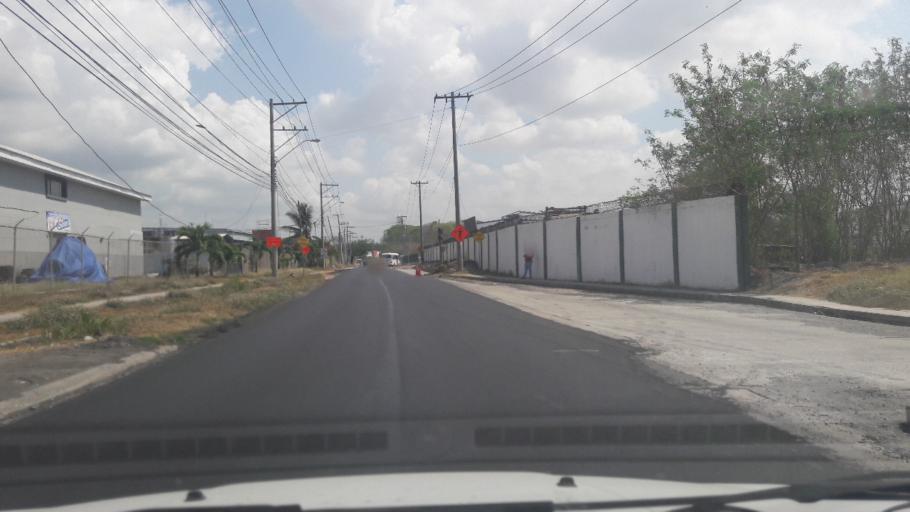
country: PA
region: Panama
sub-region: Distrito de Panama
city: Ancon
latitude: 8.9692
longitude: -79.5476
